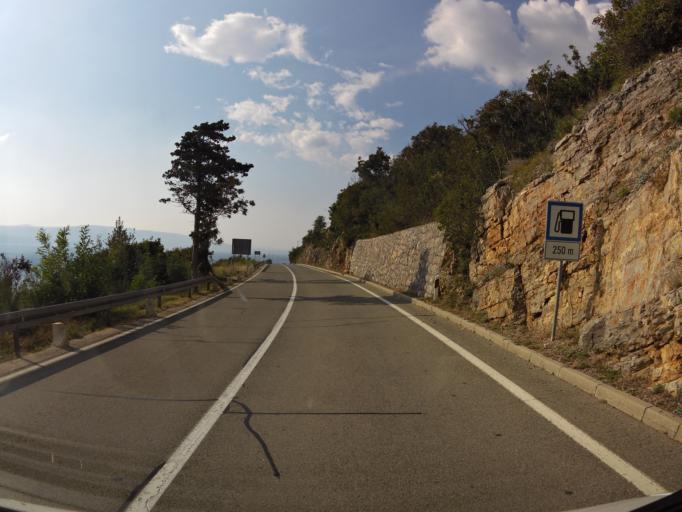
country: HR
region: Licko-Senjska
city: Senj
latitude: 44.9815
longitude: 14.9100
